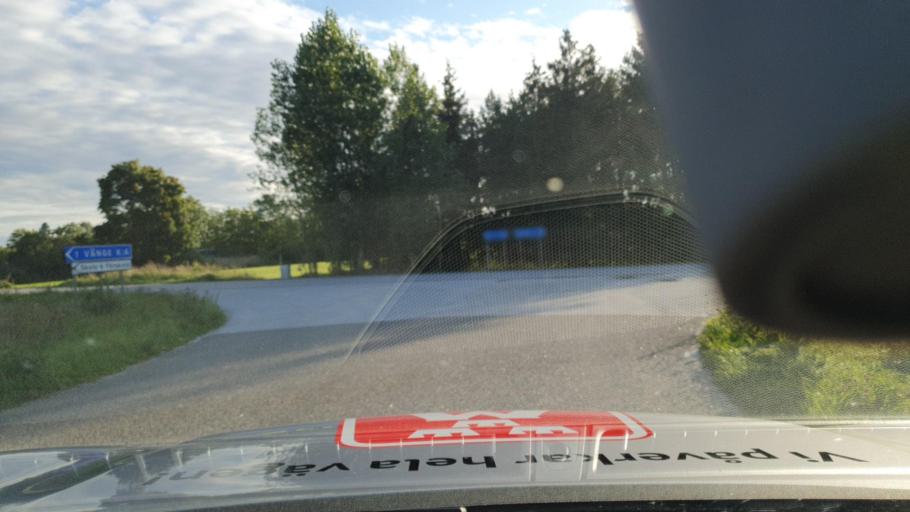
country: SE
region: Gotland
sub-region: Gotland
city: Hemse
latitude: 57.4441
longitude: 18.5139
